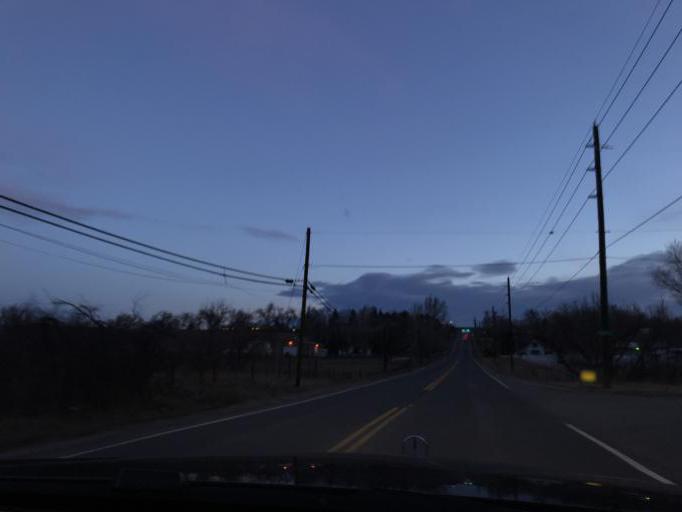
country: US
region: Colorado
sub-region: Jefferson County
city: Applewood
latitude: 39.8384
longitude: -105.1651
